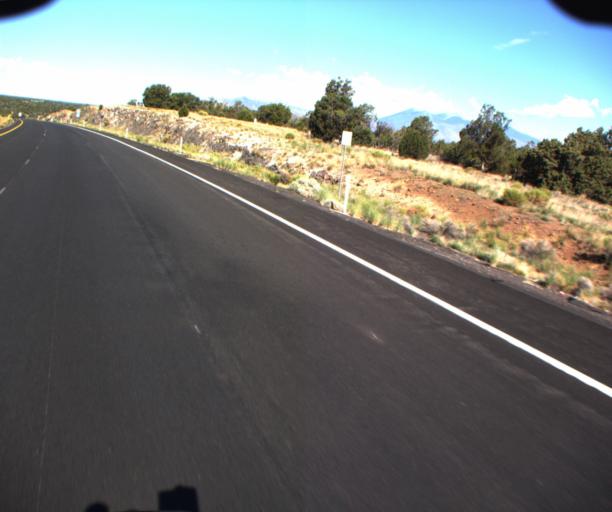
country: US
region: Arizona
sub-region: Coconino County
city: Flagstaff
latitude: 35.2030
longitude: -111.4141
